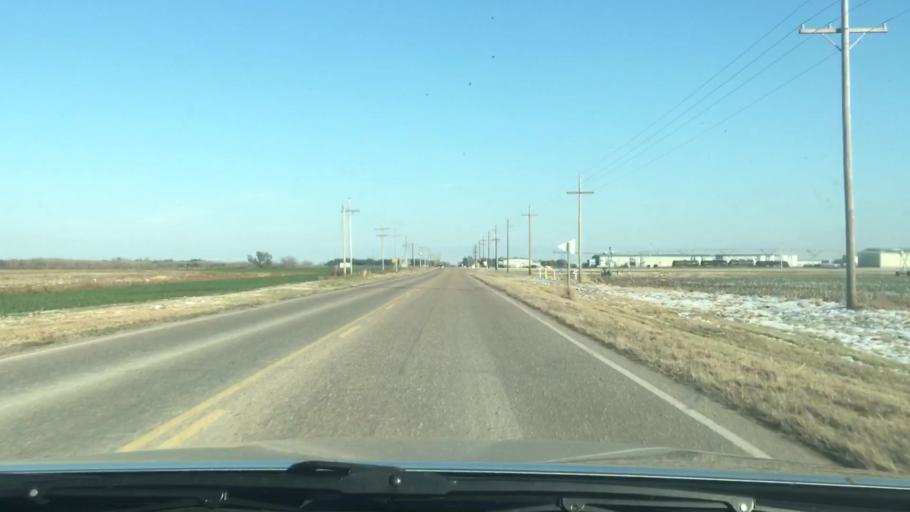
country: US
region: Kansas
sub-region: Rice County
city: Lyons
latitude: 38.2896
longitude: -98.1990
